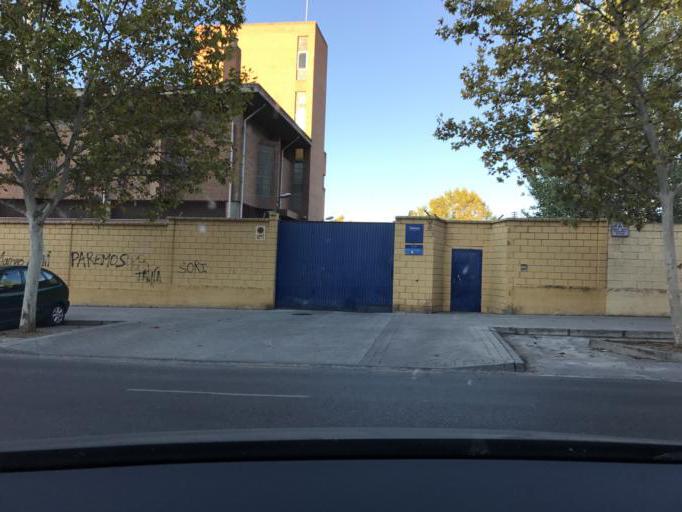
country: ES
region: Andalusia
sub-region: Provincia de Granada
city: Granada
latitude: 37.2011
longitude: -3.6042
